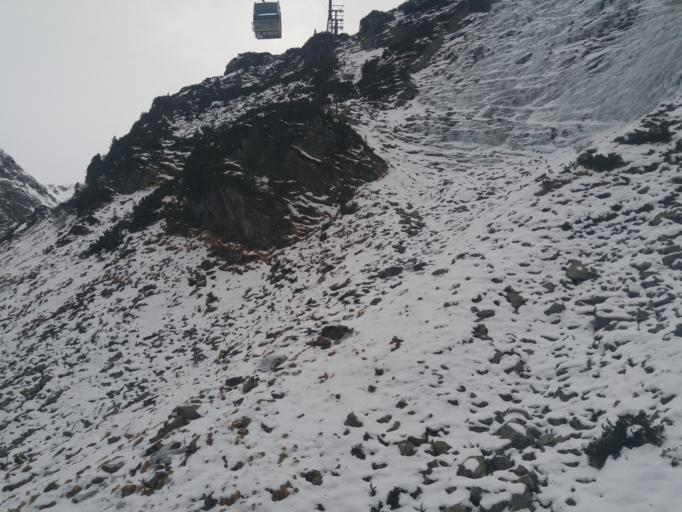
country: AT
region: Salzburg
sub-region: Politischer Bezirk Zell am See
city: Niedernsill
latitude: 47.1531
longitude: 12.6240
